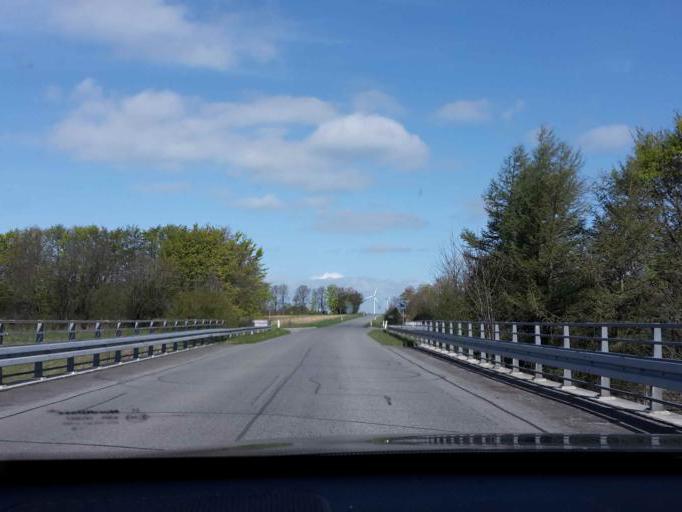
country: DK
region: South Denmark
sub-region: Vejen Kommune
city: Vejen
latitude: 55.5451
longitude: 9.0821
